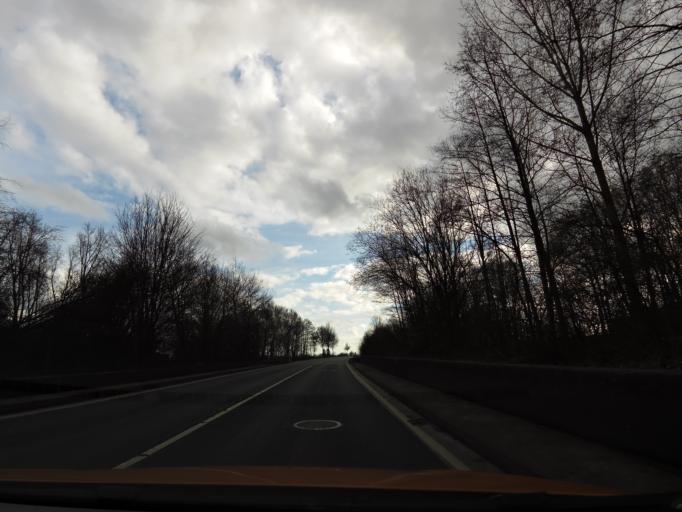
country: DE
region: Lower Saxony
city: Bassum
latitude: 52.8543
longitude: 8.7530
